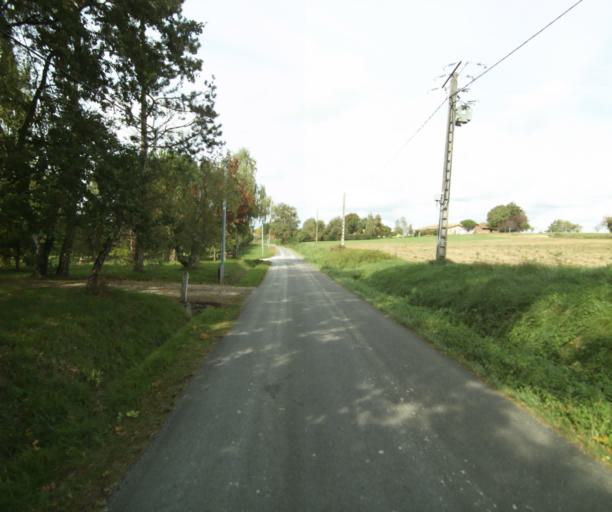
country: FR
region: Midi-Pyrenees
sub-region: Departement du Gers
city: Eauze
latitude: 43.8356
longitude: 0.1153
